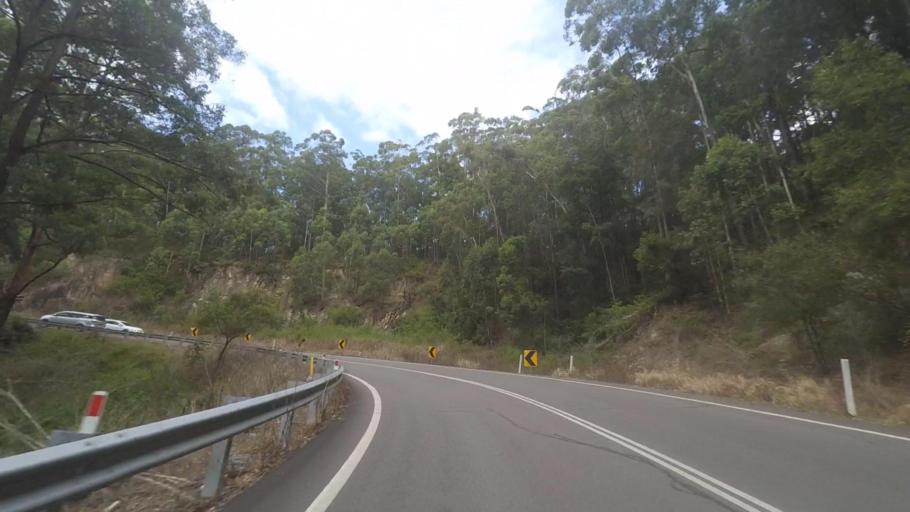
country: AU
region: New South Wales
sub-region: Great Lakes
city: Bulahdelah
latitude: -32.3944
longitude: 152.2455
